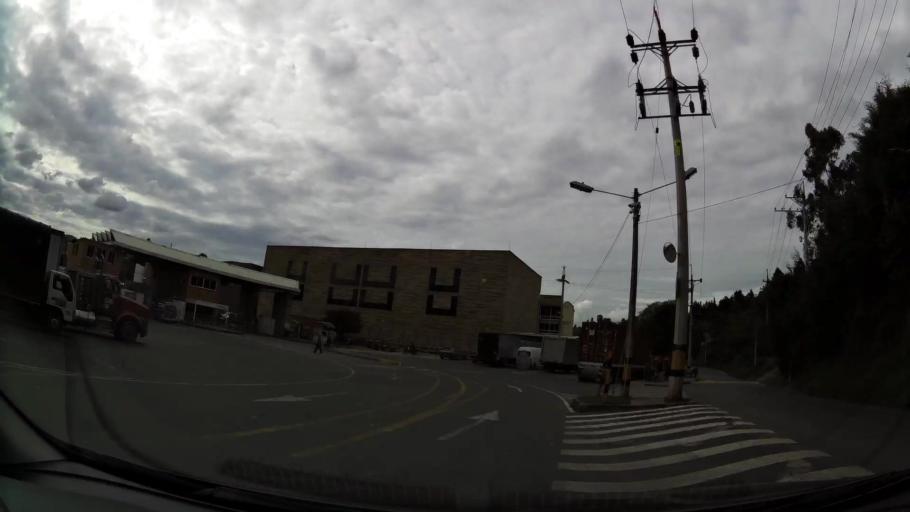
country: CO
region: Antioquia
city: Rionegro
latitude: 6.1574
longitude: -75.4119
